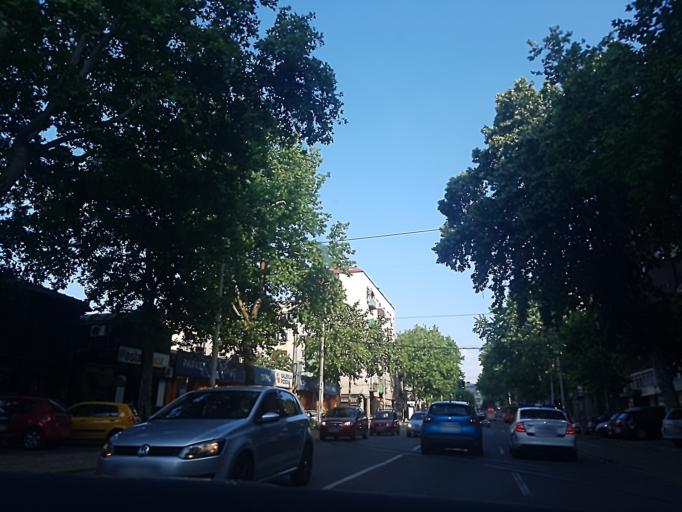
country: RS
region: Central Serbia
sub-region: Belgrade
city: Stari Grad
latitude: 44.8218
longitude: 20.4630
